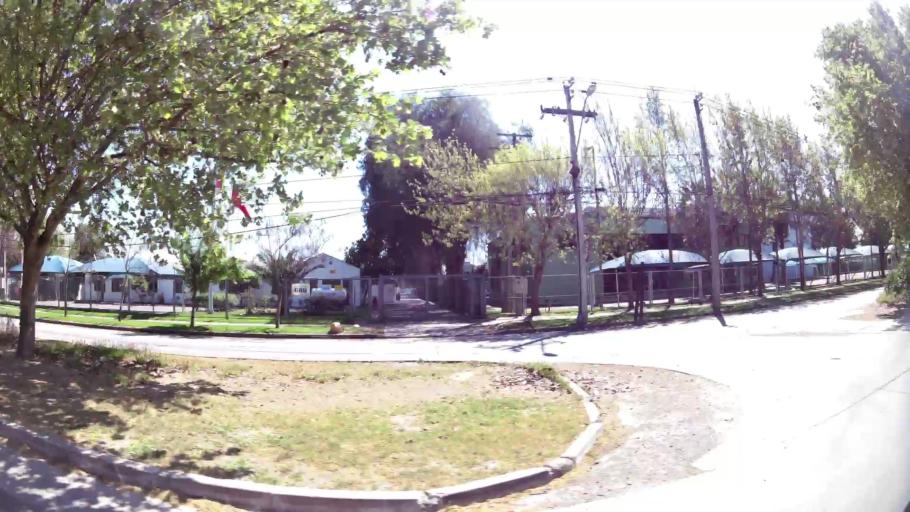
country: CL
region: Santiago Metropolitan
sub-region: Provincia de Santiago
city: Lo Prado
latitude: -33.3809
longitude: -70.7445
